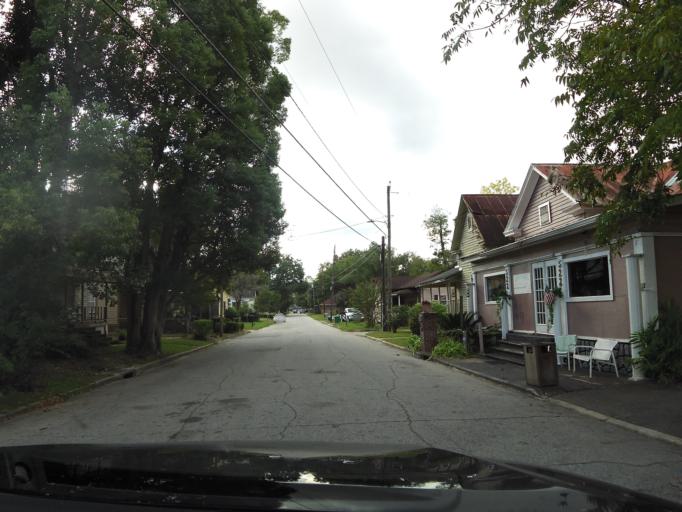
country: US
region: Georgia
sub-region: Lowndes County
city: Valdosta
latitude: 30.8322
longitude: -83.2861
